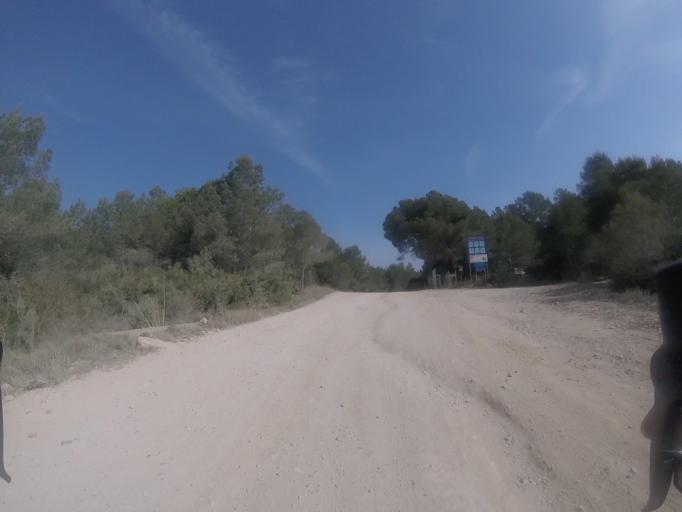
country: ES
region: Valencia
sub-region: Provincia de Castello
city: Alcoceber
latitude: 40.2655
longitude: 0.2998
